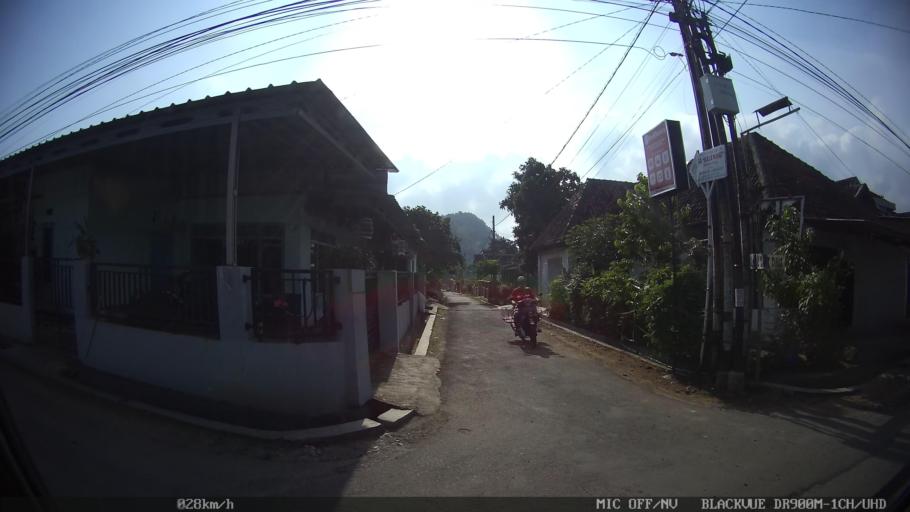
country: ID
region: Lampung
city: Kedaton
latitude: -5.3900
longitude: 105.2635
